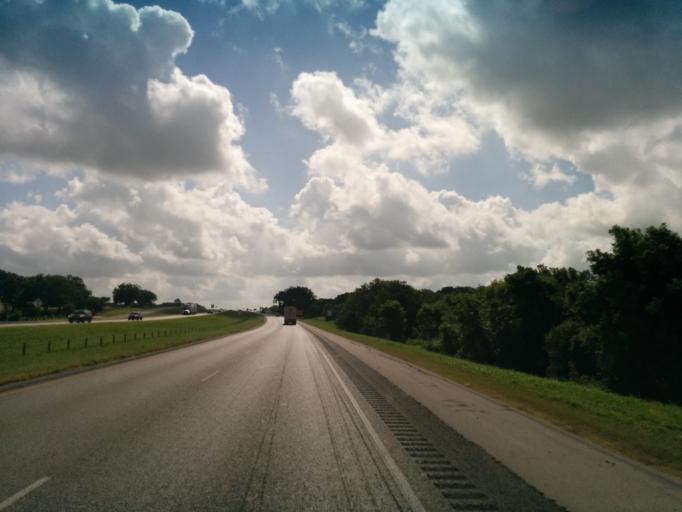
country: US
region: Texas
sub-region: Fayette County
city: Schulenburg
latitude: 29.6905
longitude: -96.9214
